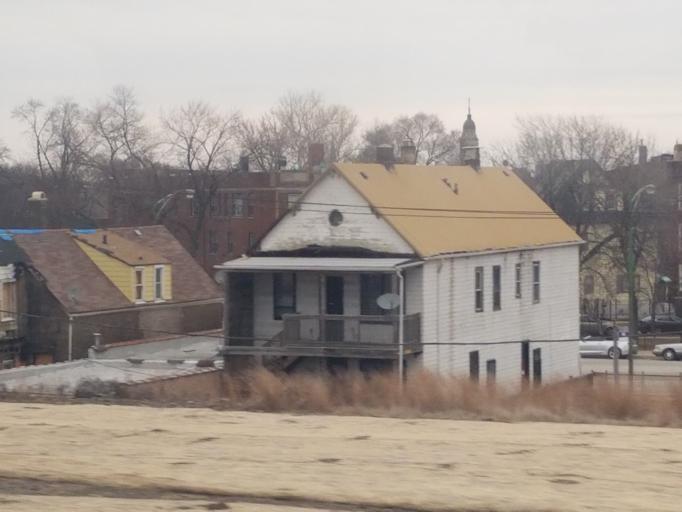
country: US
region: Indiana
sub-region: Lake County
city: Whiting
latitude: 41.7289
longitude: -87.5539
